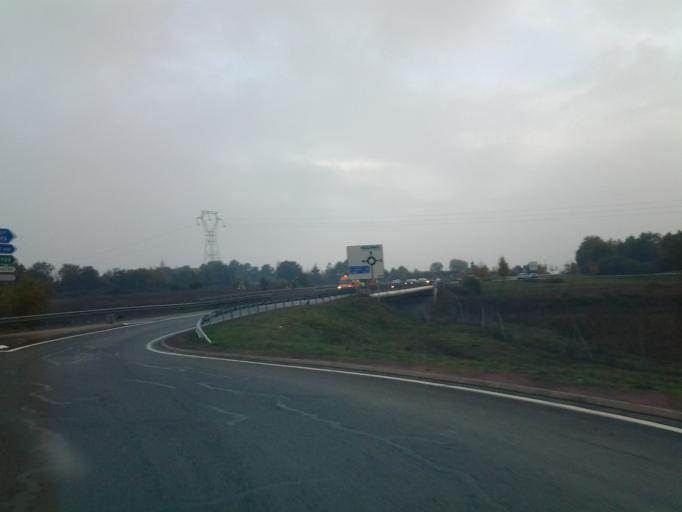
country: FR
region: Pays de la Loire
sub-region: Departement de la Vendee
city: Nesmy
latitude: 46.6371
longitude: -1.3973
